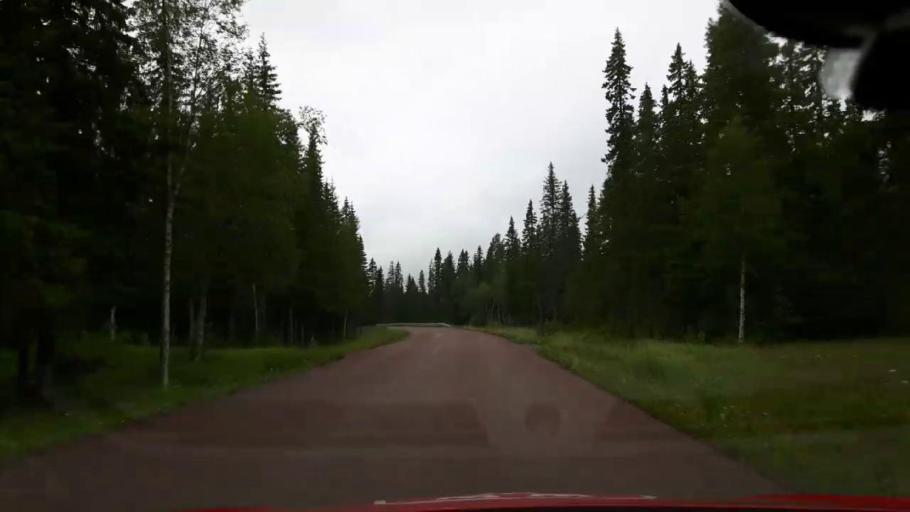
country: SE
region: Jaemtland
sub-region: Krokoms Kommun
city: Valla
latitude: 63.3904
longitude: 13.8438
